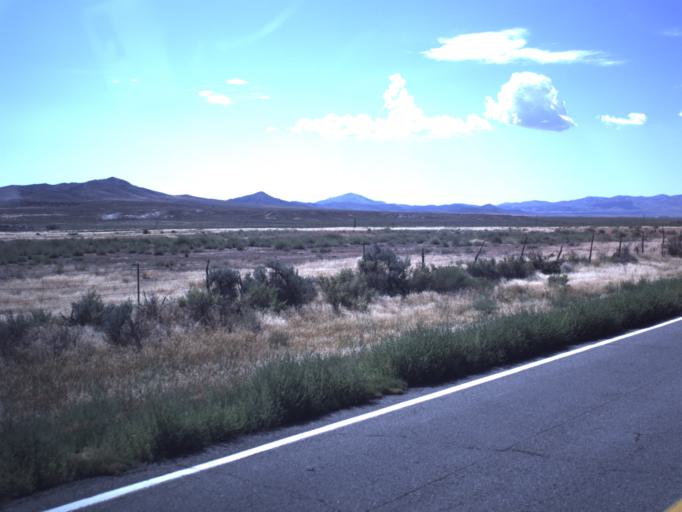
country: US
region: Utah
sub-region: Tooele County
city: Tooele
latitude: 40.1796
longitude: -112.4247
